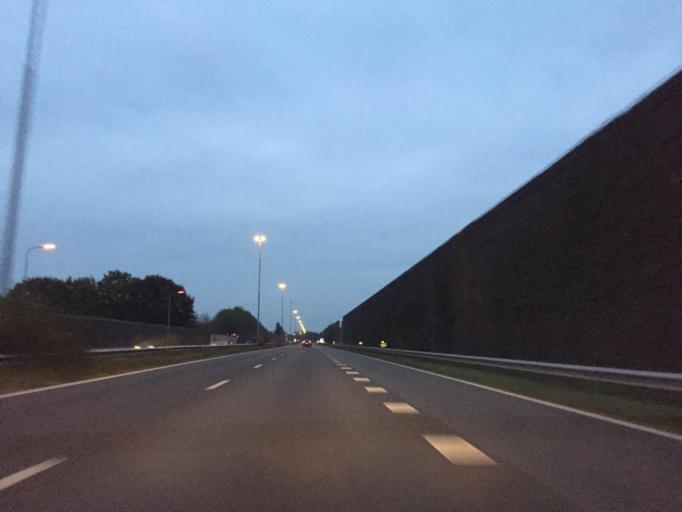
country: NL
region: North Brabant
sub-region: Gemeente Heusden
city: Heusden
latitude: 51.6935
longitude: 5.2024
